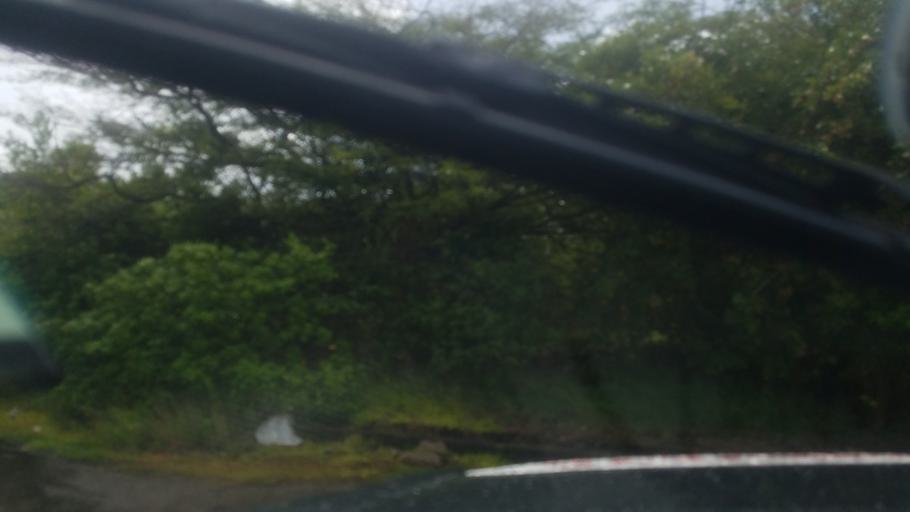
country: LC
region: Laborie Quarter
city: Laborie
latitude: 13.7344
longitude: -60.9737
